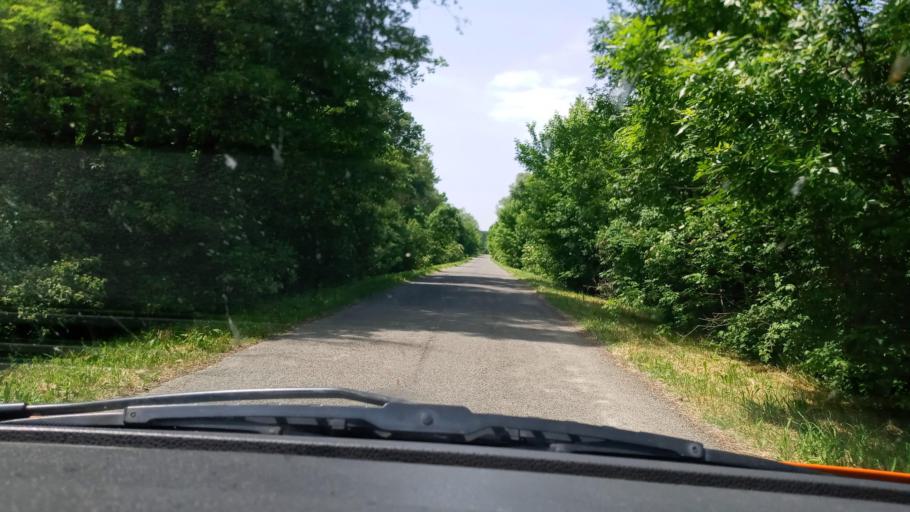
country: HU
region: Baranya
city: Sellye
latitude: 45.8078
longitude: 17.8738
